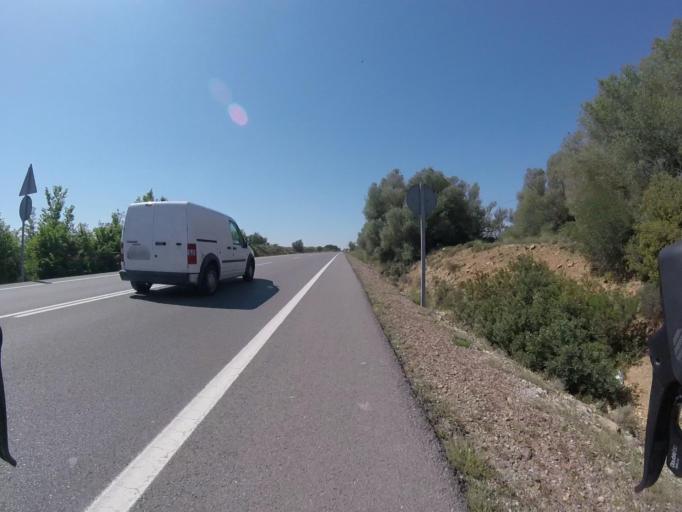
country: ES
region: Valencia
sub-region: Provincia de Castello
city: Benlloch
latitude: 40.2249
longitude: 0.0512
